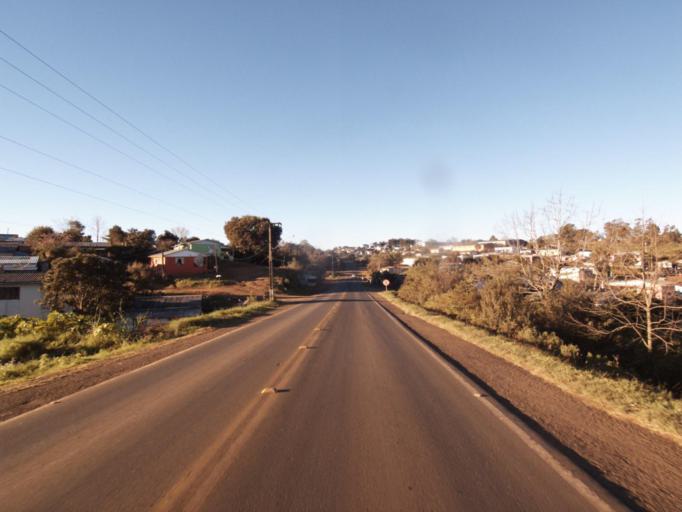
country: AR
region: Misiones
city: Bernardo de Irigoyen
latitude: -26.2628
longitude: -53.6222
